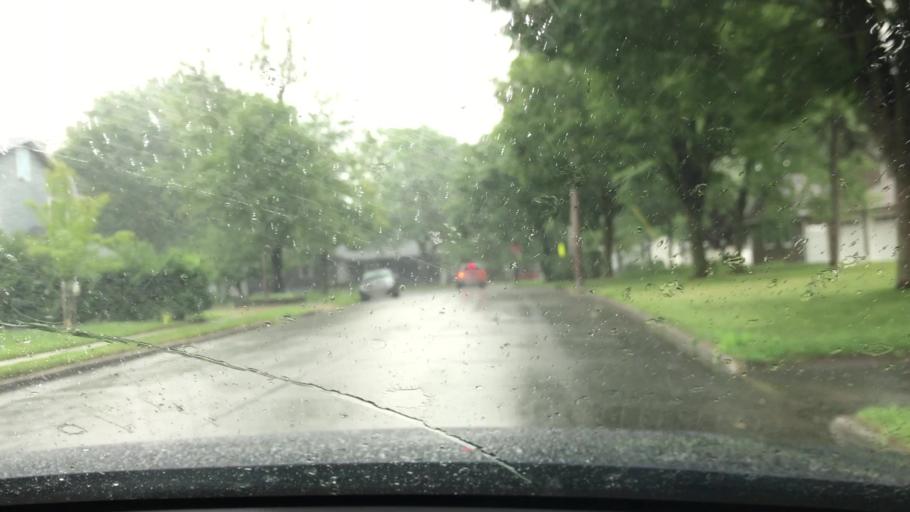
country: US
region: New Jersey
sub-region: Bergen County
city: Paramus
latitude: 40.9677
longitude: -74.0831
